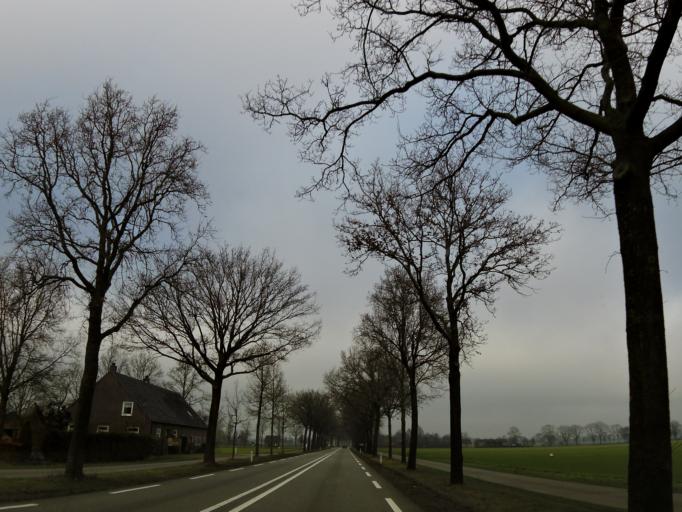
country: NL
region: North Brabant
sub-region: Gemeente Mill en Sint Hubert
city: Wilbertoord
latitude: 51.5901
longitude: 5.7609
